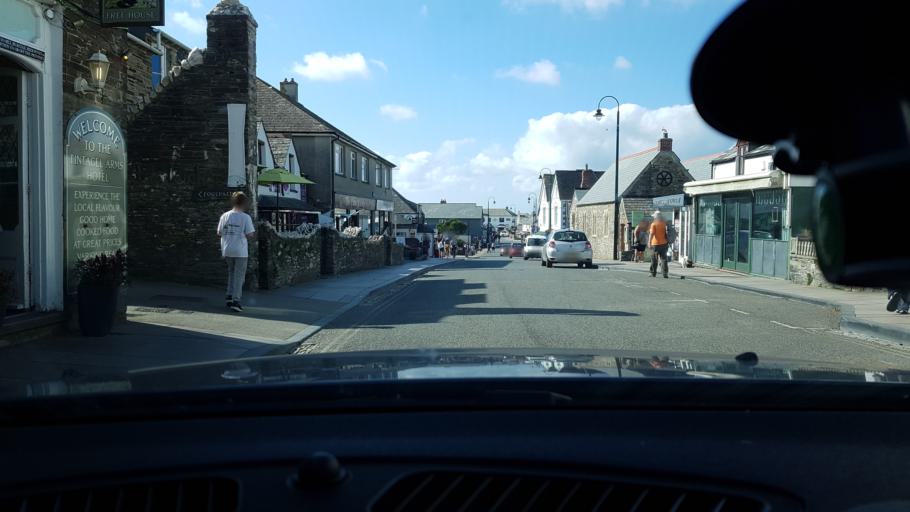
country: GB
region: England
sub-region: Cornwall
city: Tintagel
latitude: 50.6630
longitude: -4.7502
